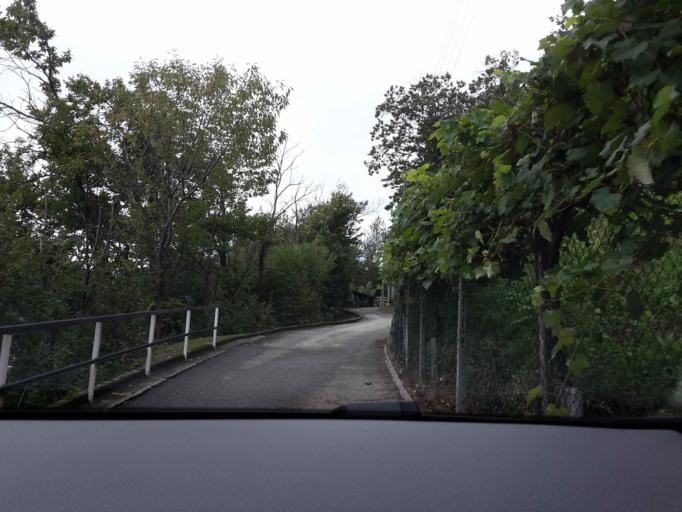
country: CH
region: Ticino
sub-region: Bellinzona District
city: Sementina
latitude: 46.1827
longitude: 8.9781
